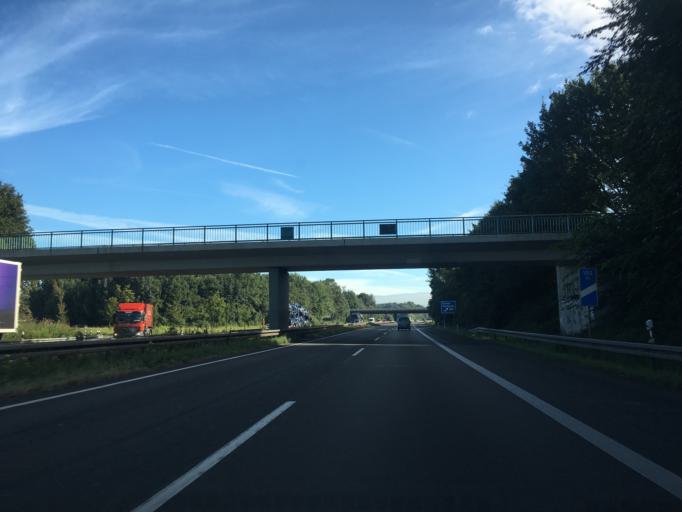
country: DE
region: North Rhine-Westphalia
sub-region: Regierungsbezirk Munster
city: Greven
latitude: 52.0817
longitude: 7.6412
